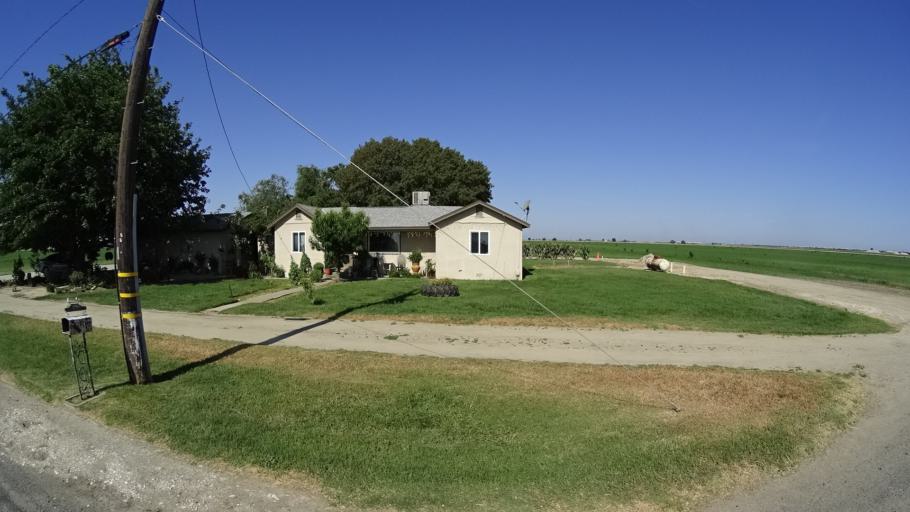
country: US
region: California
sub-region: Kings County
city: Home Garden
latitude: 36.2285
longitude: -119.5472
